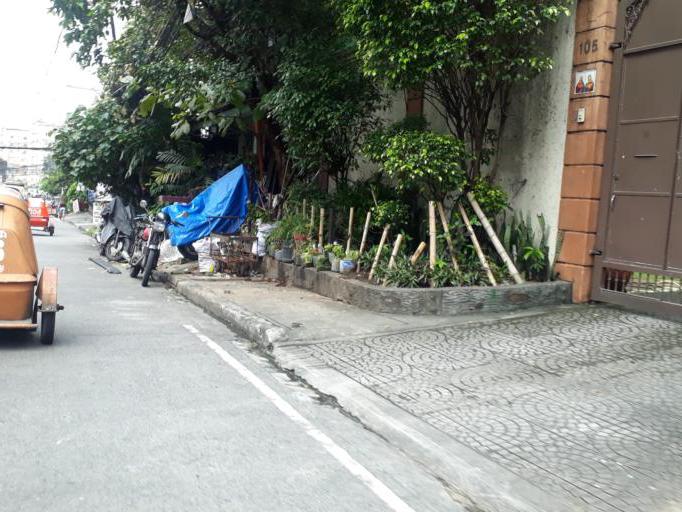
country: PH
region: Metro Manila
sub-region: San Juan
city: San Juan
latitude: 14.6170
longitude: 121.0485
